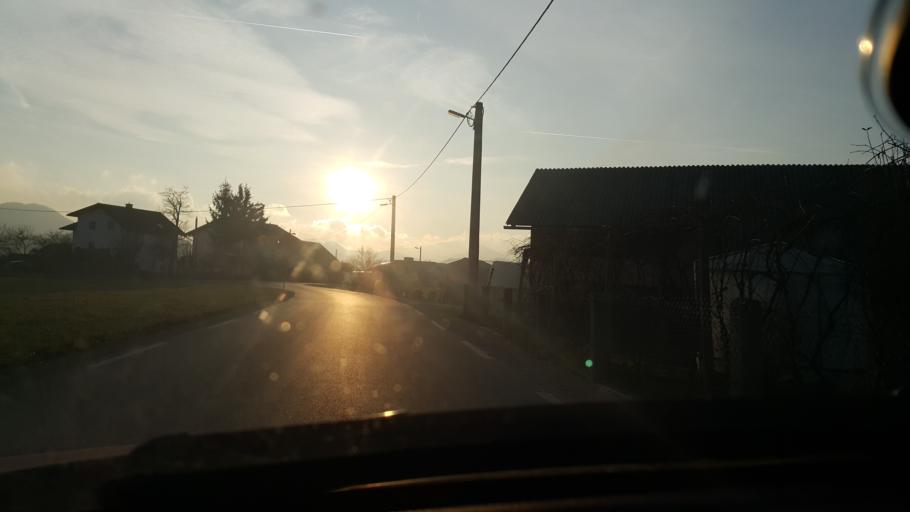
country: SI
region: Celje
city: Ljubecna
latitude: 46.2486
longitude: 15.3140
